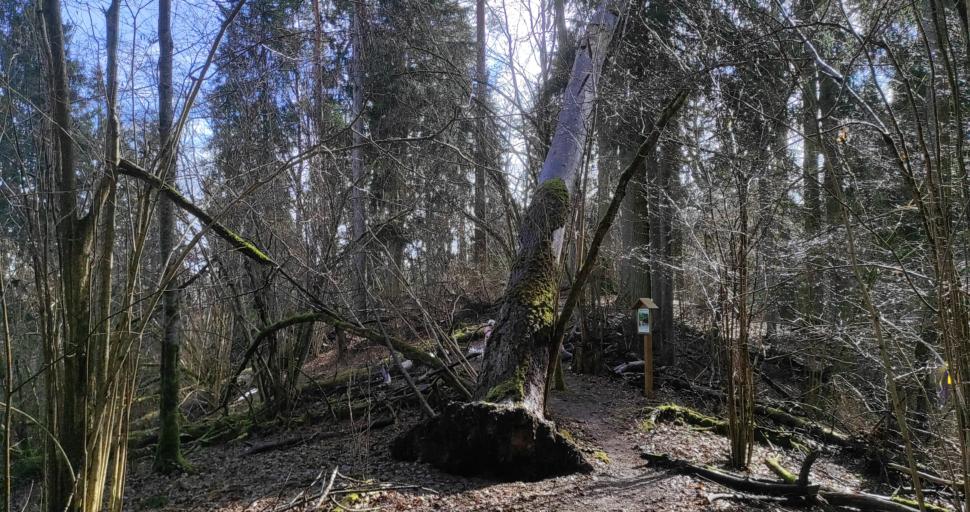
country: LV
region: Tukuma Rajons
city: Tukums
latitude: 57.1169
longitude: 23.0390
